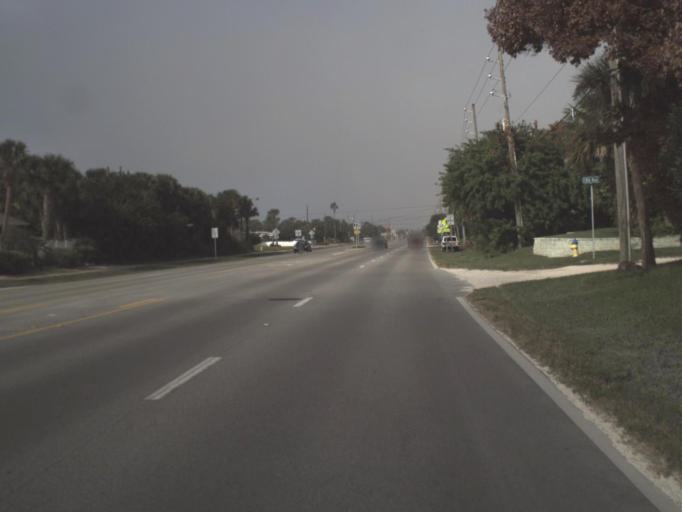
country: US
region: Florida
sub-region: Volusia County
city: Edgewater
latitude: 29.0206
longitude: -80.8864
